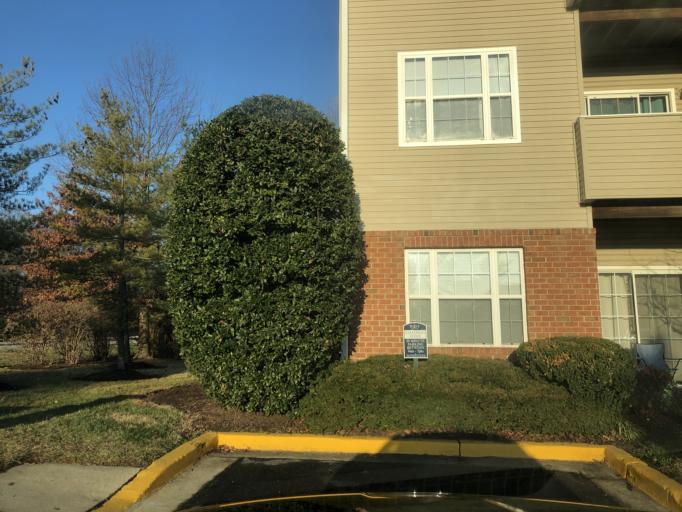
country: US
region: Maryland
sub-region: Anne Arundel County
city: Odenton
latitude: 39.1002
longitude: -76.7157
